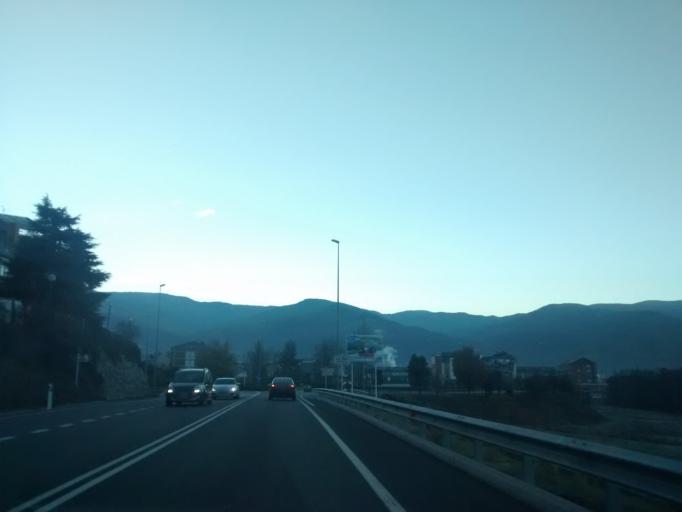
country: ES
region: Catalonia
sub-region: Provincia de Lleida
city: la Seu d'Urgell
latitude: 42.3638
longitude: 1.4557
